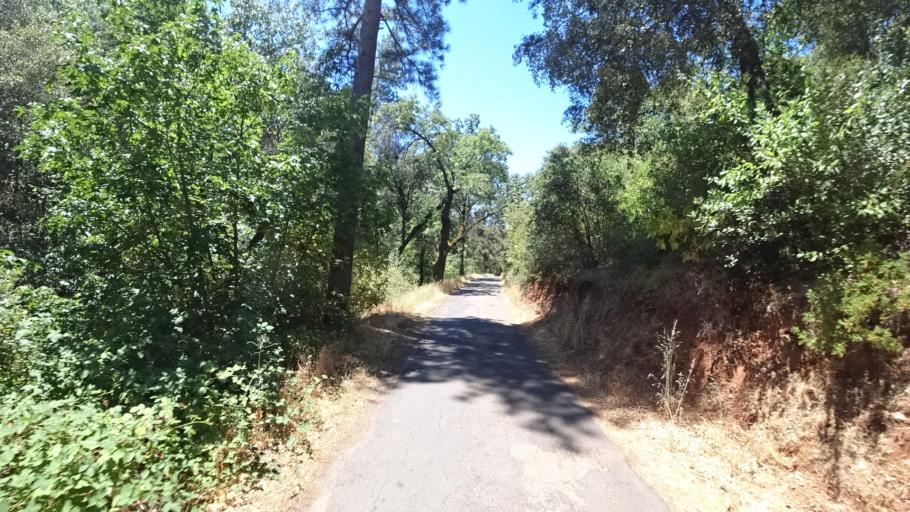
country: US
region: California
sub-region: Calaveras County
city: Forest Meadows
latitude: 38.1443
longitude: -120.4156
